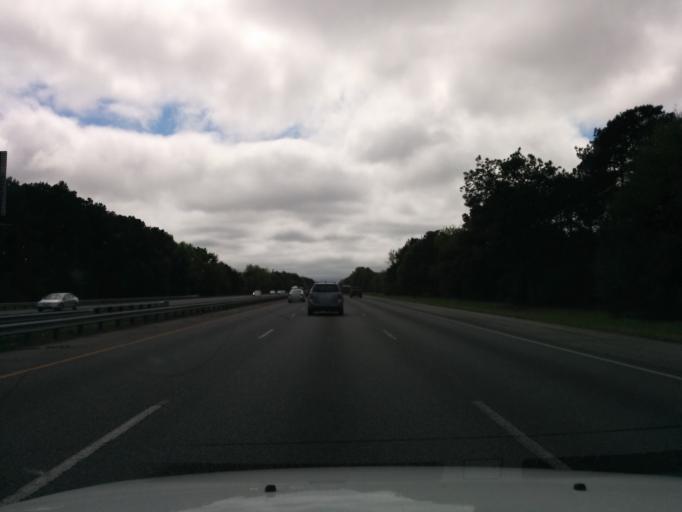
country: US
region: Georgia
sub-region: Chatham County
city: Georgetown
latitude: 32.0425
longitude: -81.2621
